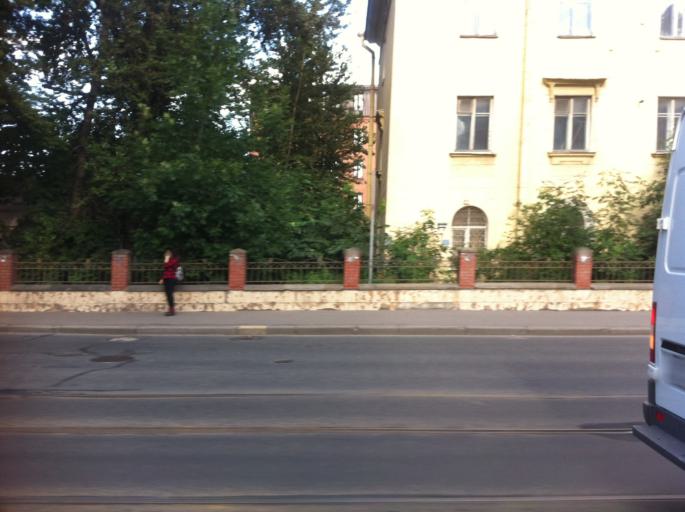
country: RU
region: St.-Petersburg
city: Admiralteisky
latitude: 59.9074
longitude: 30.2753
